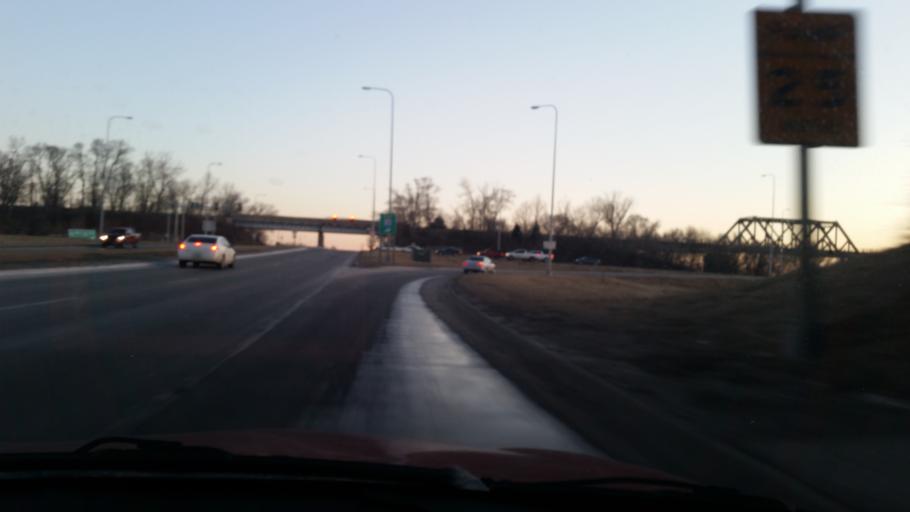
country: US
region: Nebraska
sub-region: Douglas County
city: Ralston
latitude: 41.2235
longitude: -96.0048
